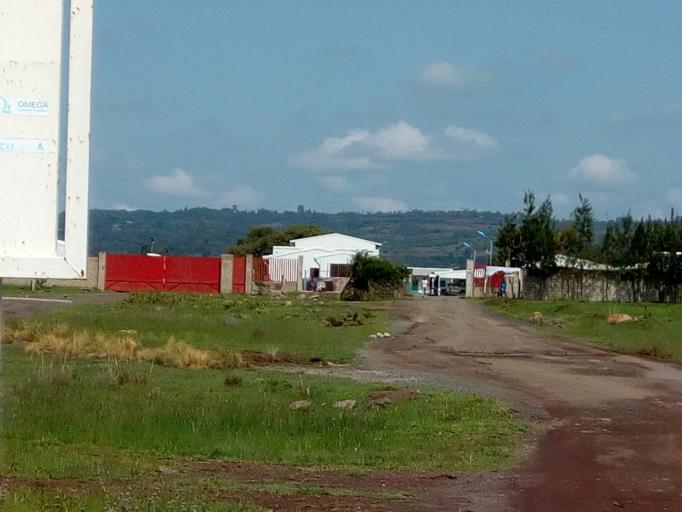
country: ET
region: Oromiya
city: Waliso
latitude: 8.5572
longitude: 37.9494
